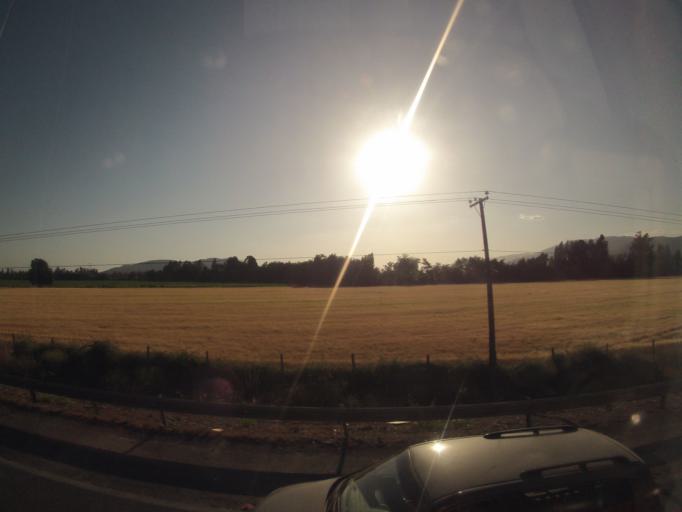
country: CL
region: O'Higgins
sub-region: Provincia de Colchagua
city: Chimbarongo
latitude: -34.5832
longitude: -70.9664
